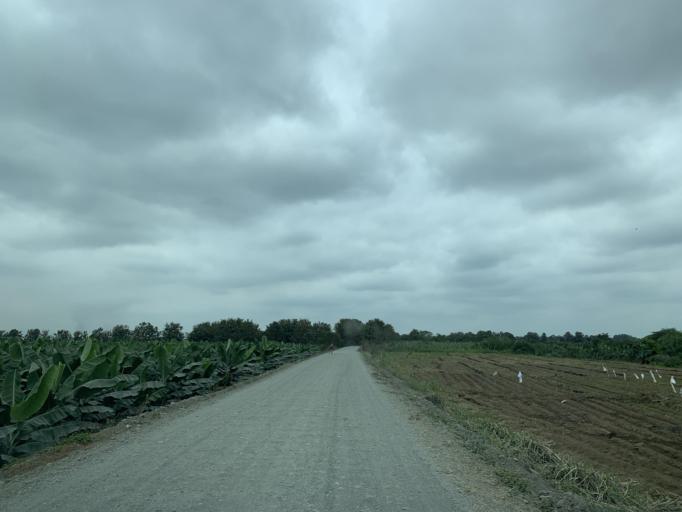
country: EC
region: Guayas
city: Coronel Marcelino Mariduena
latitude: -2.3285
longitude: -79.4574
